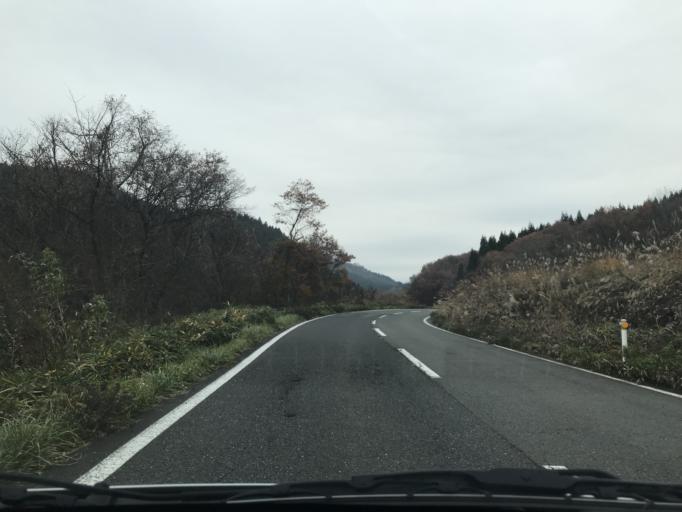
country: JP
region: Iwate
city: Kitakami
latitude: 39.2689
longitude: 141.1799
